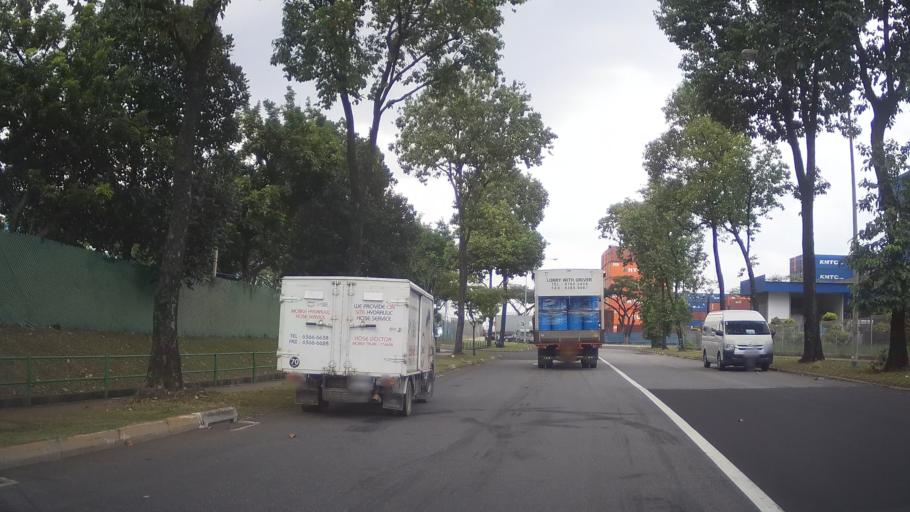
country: MY
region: Johor
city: Johor Bahru
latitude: 1.3060
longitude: 103.6645
